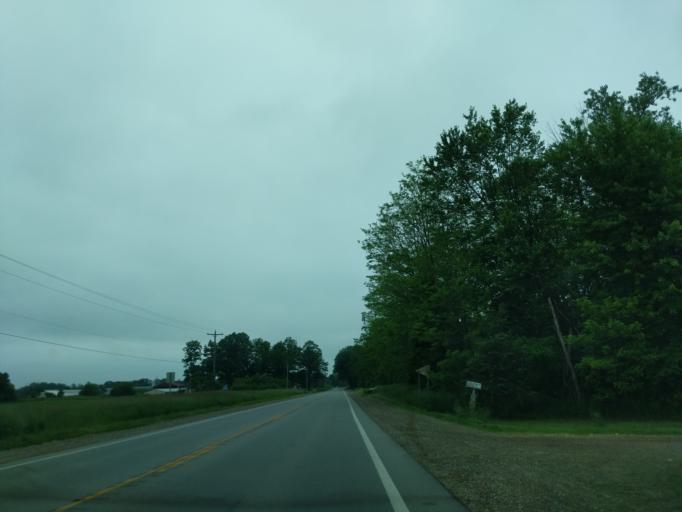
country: US
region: Michigan
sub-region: Branch County
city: Quincy
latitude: 41.9503
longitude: -84.8032
